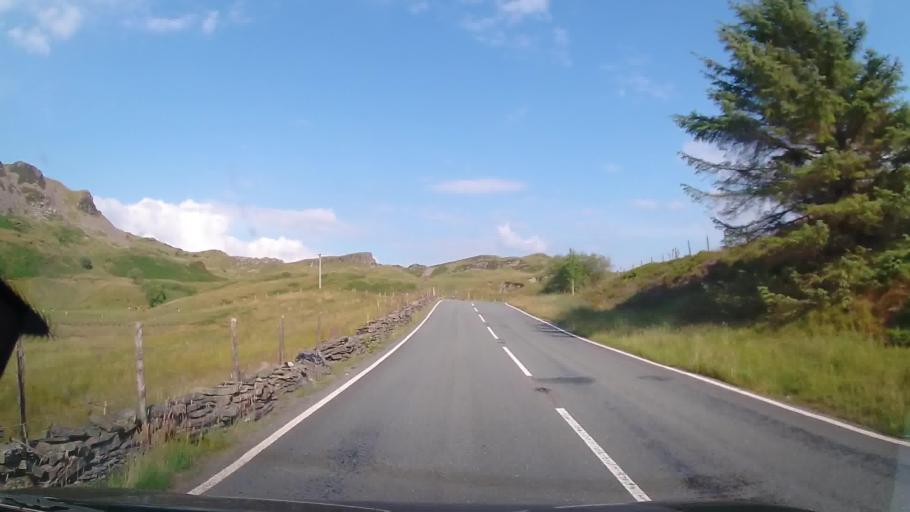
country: GB
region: Wales
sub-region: Gwynedd
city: Ffestiniog
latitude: 52.9621
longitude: -3.8989
